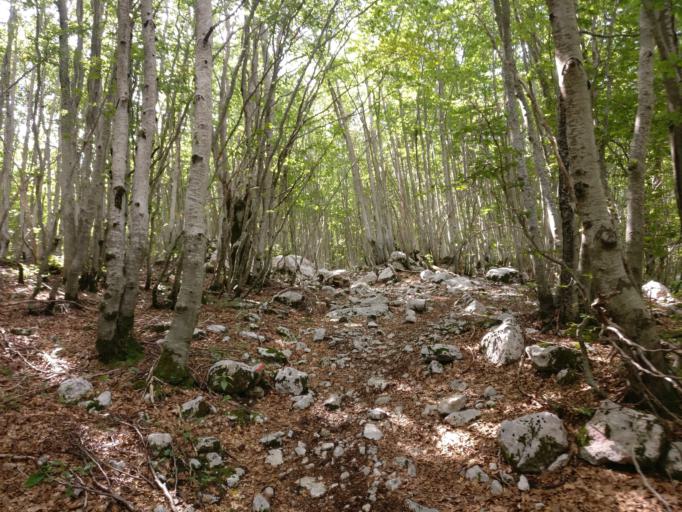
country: ME
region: Kotor
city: Kotor
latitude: 42.4091
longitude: 18.8396
